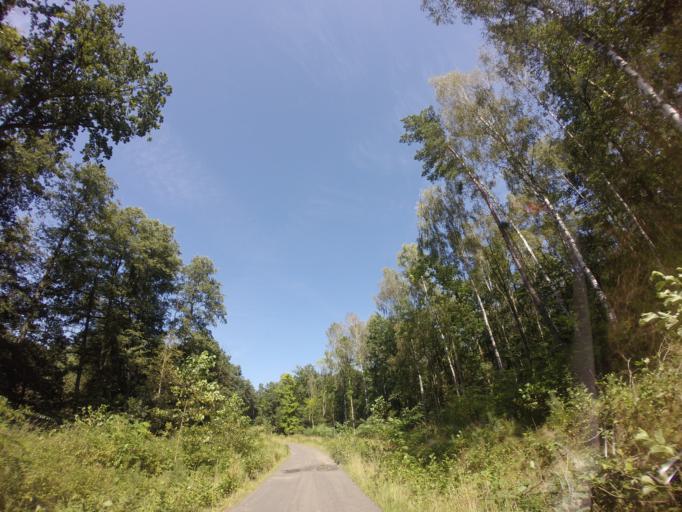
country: PL
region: West Pomeranian Voivodeship
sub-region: Powiat choszczenski
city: Choszczno
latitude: 53.1922
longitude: 15.3641
